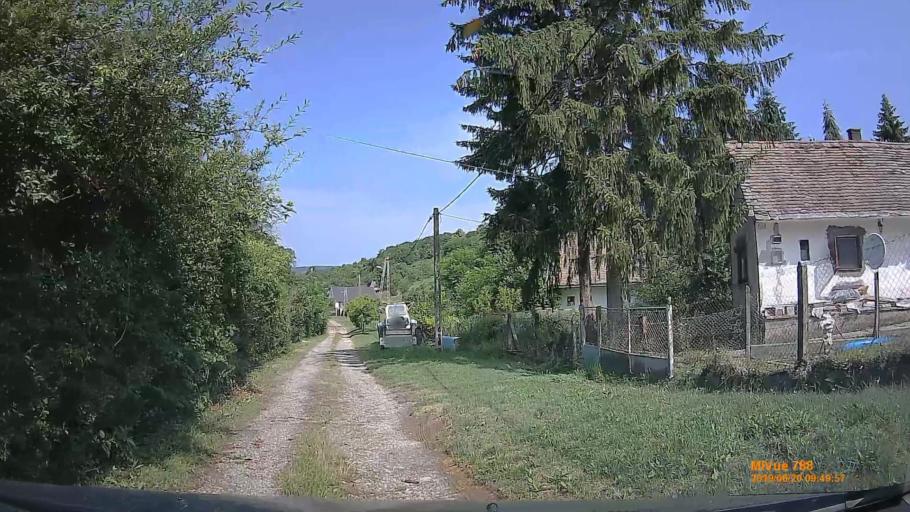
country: HU
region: Baranya
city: Pecsvarad
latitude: 46.1725
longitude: 18.4734
